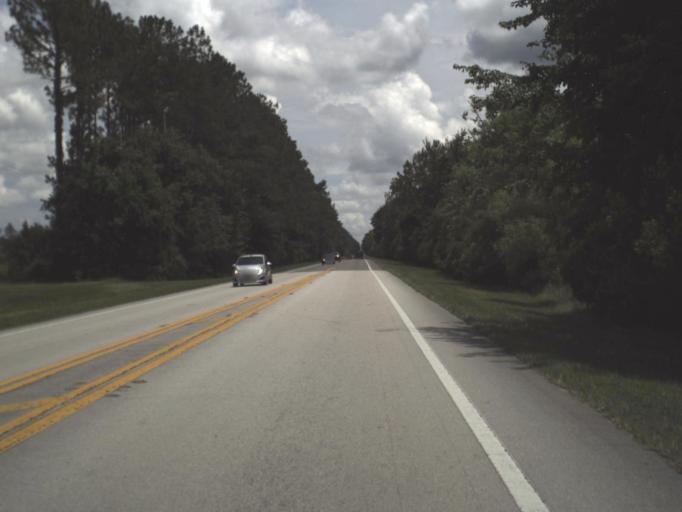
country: US
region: Florida
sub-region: Nassau County
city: Yulee
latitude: 30.6991
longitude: -81.6624
